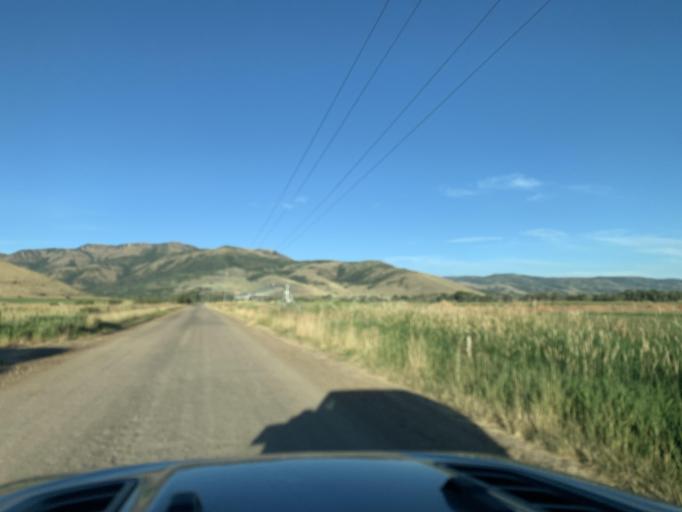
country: US
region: Utah
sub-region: Weber County
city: Wolf Creek
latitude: 41.2930
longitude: -111.7758
